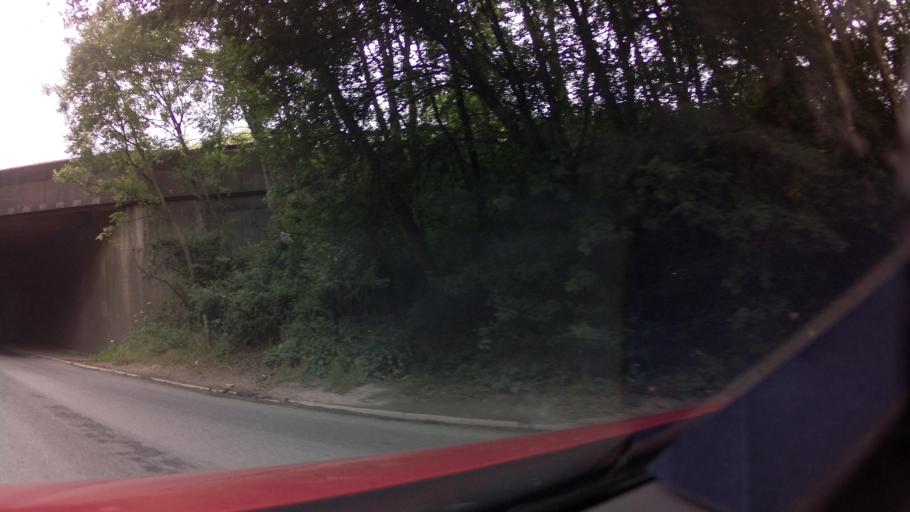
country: GB
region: England
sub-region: Wiltshire
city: Royal Wootton Bassett
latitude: 51.5588
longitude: -1.9089
